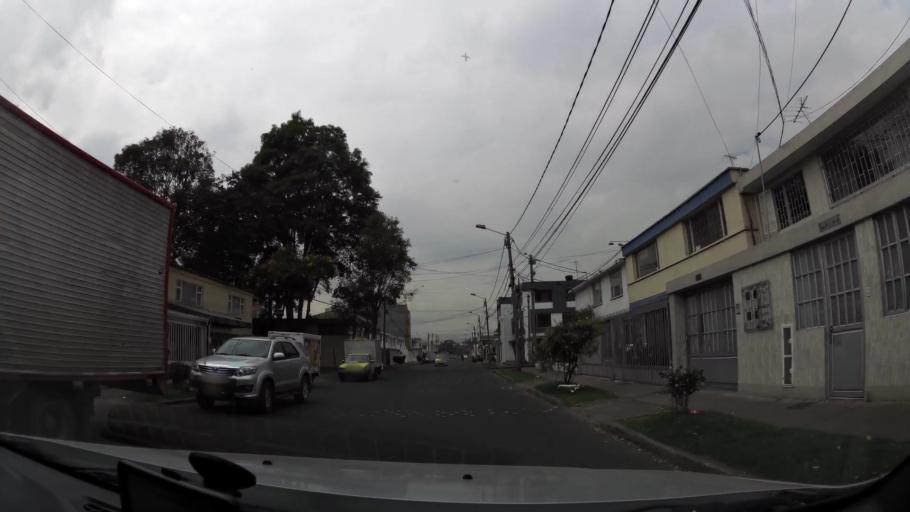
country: CO
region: Bogota D.C.
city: Barrio San Luis
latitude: 4.6882
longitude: -74.0691
